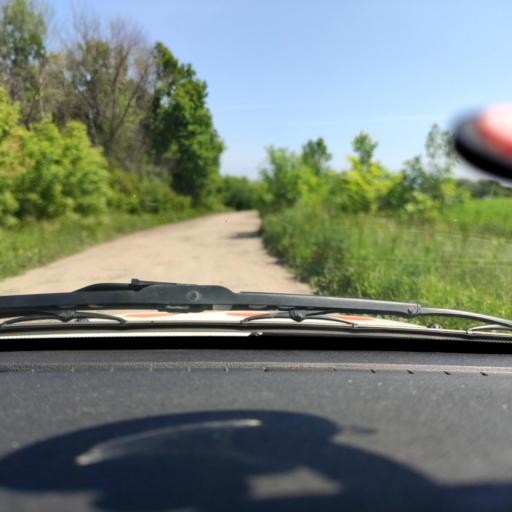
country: RU
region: Voronezj
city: Devitsa
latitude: 51.5952
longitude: 38.9822
